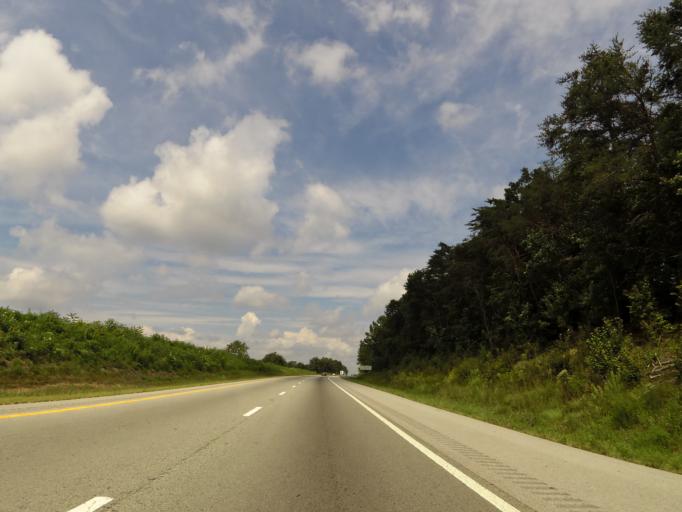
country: US
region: Tennessee
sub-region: Cumberland County
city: Fairfield Glade
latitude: 35.9322
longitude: -84.9216
